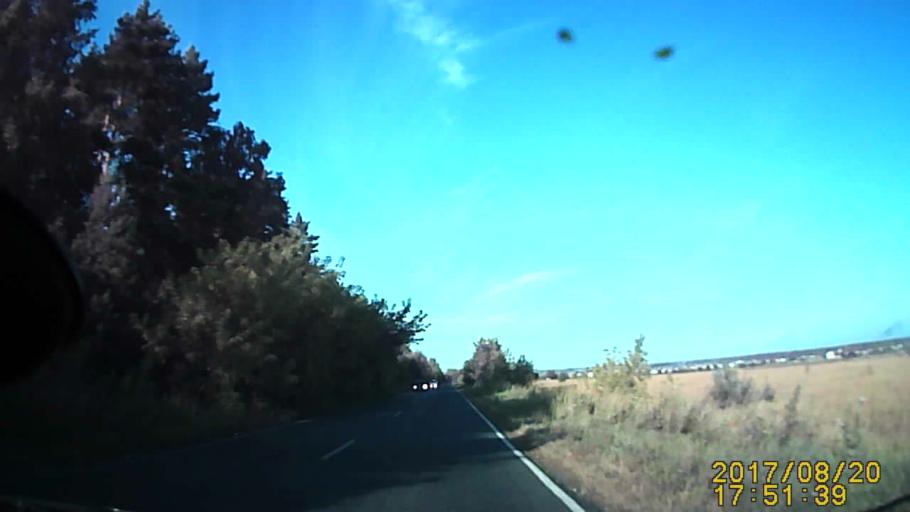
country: RU
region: Ulyanovsk
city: Cherdakly
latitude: 54.4338
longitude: 48.8192
